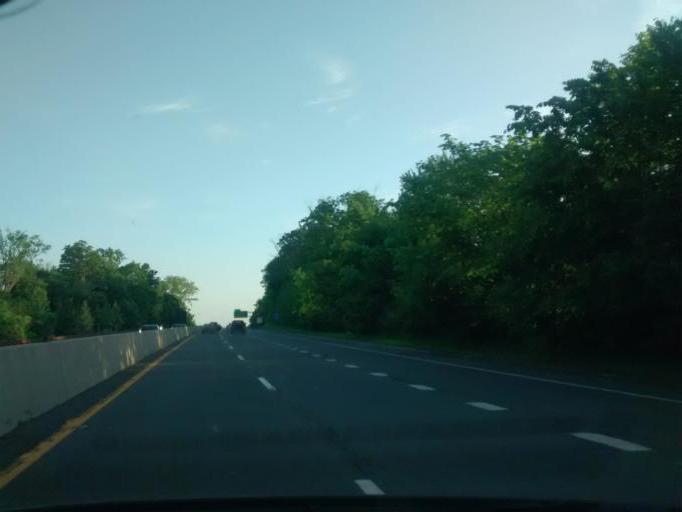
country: US
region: Connecticut
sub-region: Fairfield County
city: Glenville
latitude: 41.0356
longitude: -73.6762
